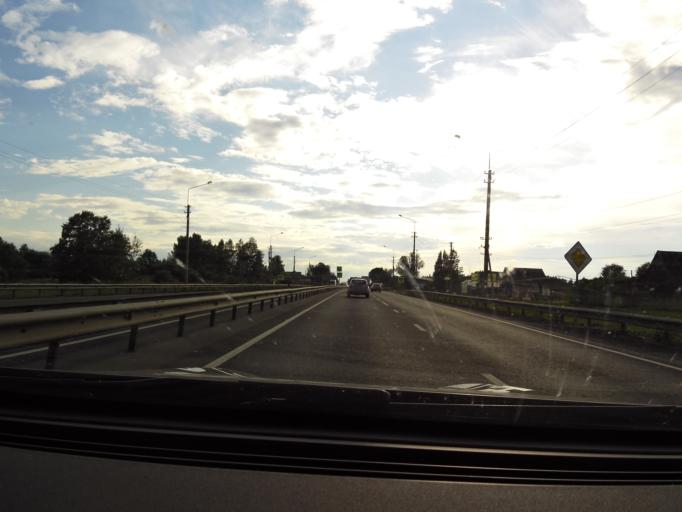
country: RU
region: Vladimir
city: Novki
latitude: 56.2019
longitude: 41.1070
